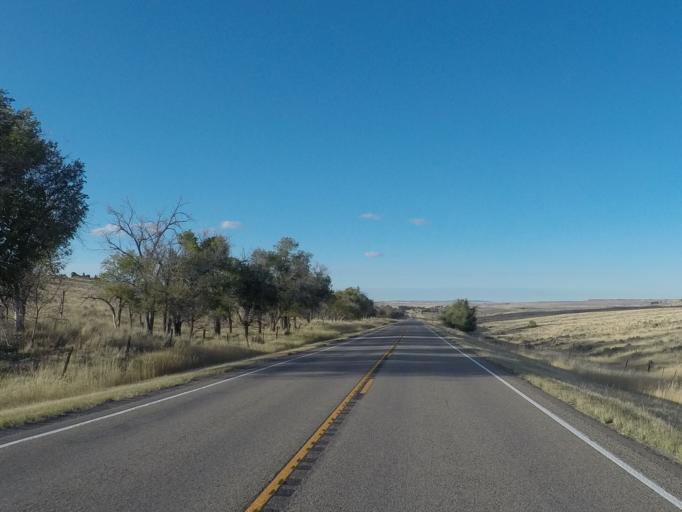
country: US
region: Montana
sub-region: Golden Valley County
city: Ryegate
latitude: 46.2422
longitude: -108.9363
